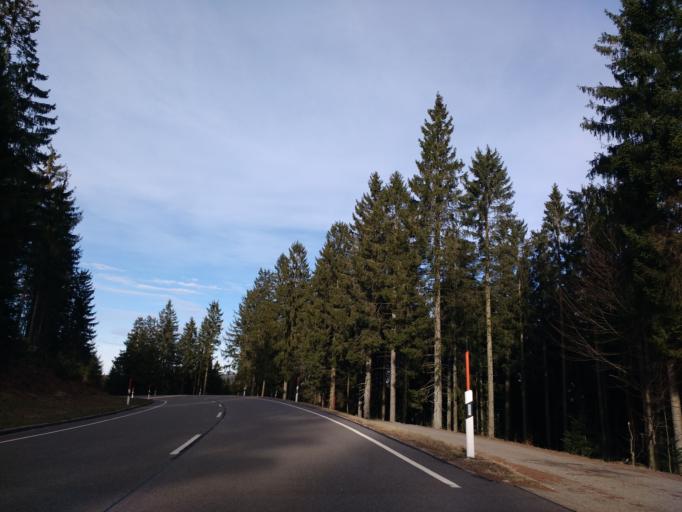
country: DE
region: Baden-Wuerttemberg
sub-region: Freiburg Region
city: Bad Peterstal-Griesbach
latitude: 48.4964
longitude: 8.2432
